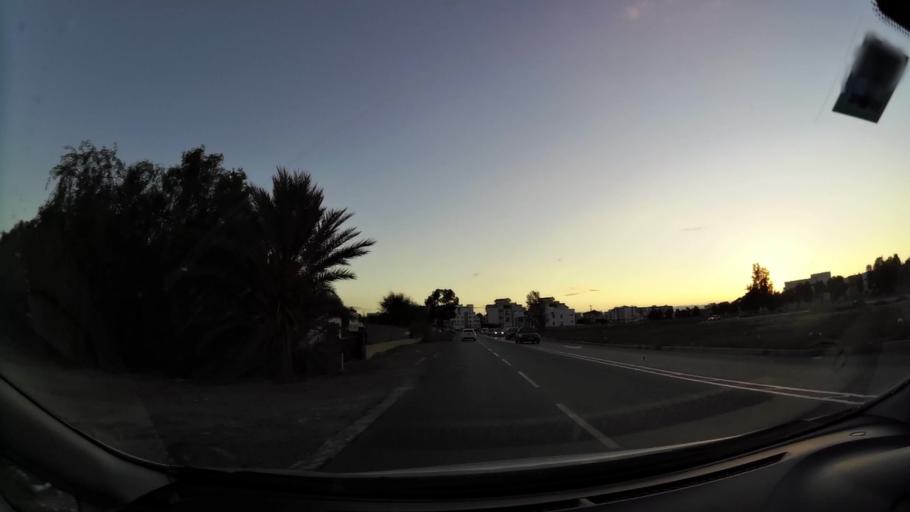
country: CY
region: Lefkosia
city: Nicosia
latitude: 35.2029
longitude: 33.3304
